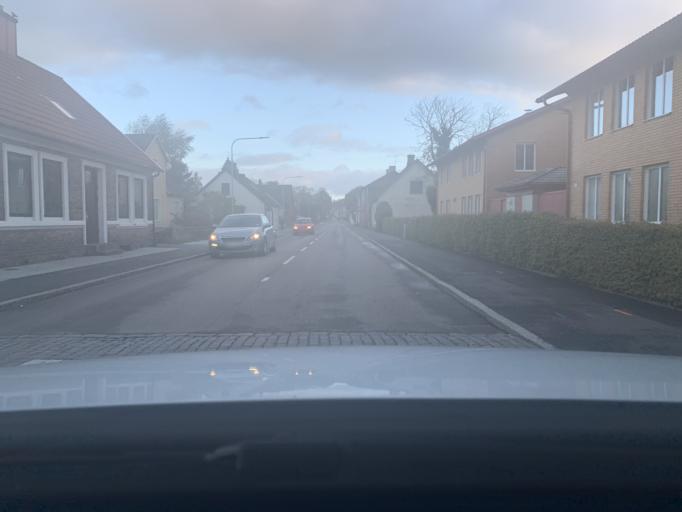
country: SE
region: Skane
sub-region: Horby Kommun
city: Hoerby
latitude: 55.8479
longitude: 13.6590
